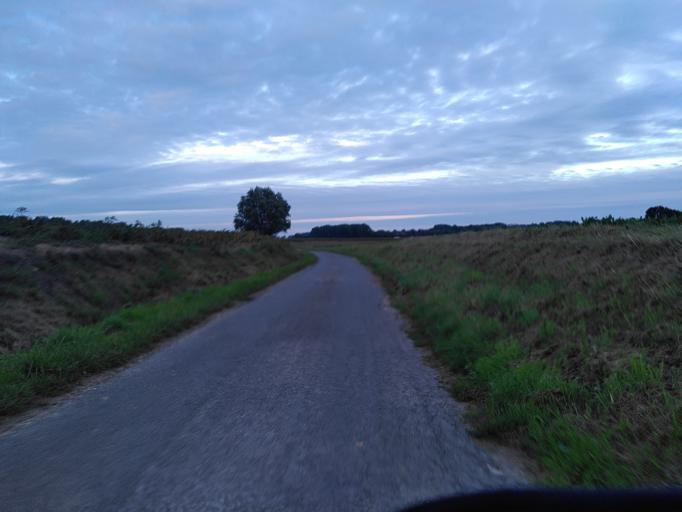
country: FR
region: Nord-Pas-de-Calais
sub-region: Departement du Pas-de-Calais
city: Therouanne
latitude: 50.6406
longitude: 2.2837
